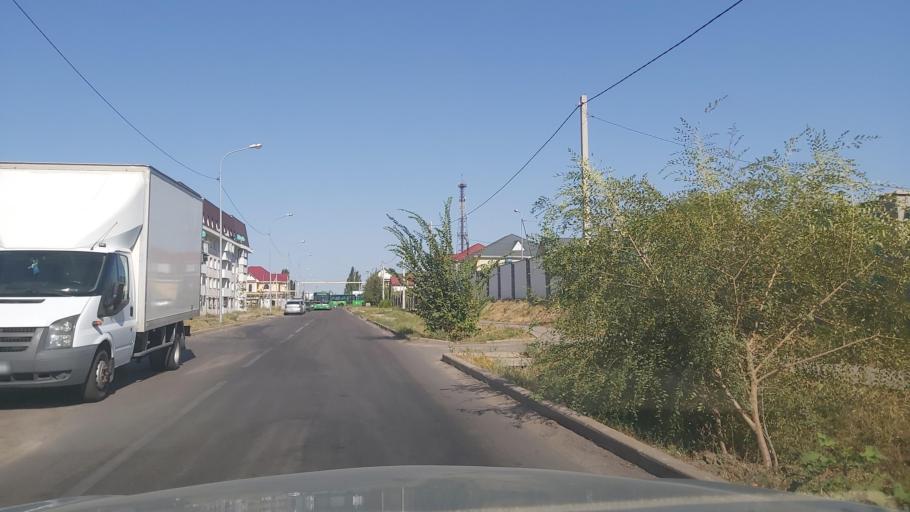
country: KZ
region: Almaty Oblysy
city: Burunday
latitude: 43.3184
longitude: 76.8395
